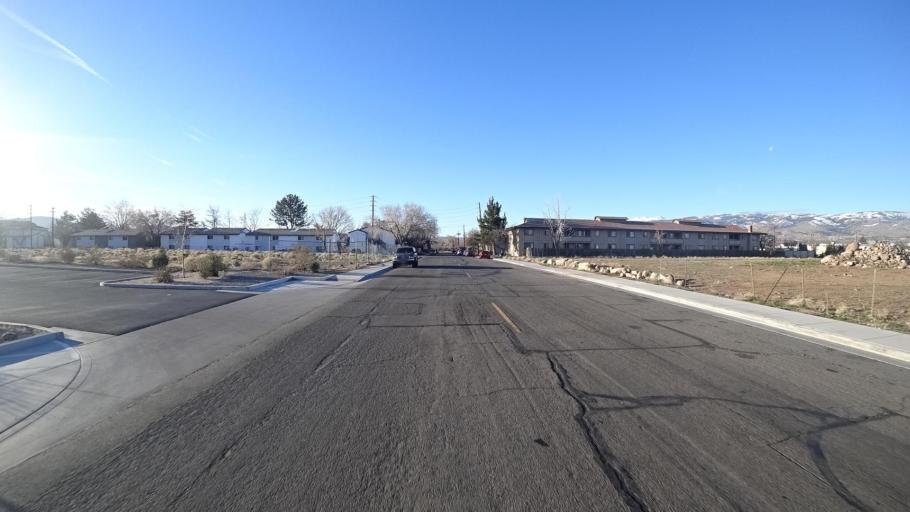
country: US
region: Nevada
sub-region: Washoe County
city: Reno
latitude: 39.5151
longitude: -119.7856
